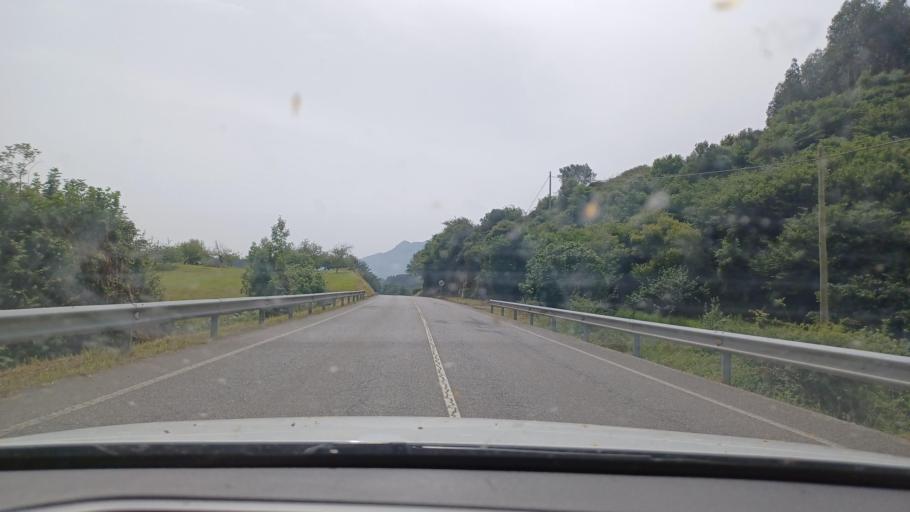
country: ES
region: Asturias
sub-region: Province of Asturias
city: Ribadesella
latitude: 43.4552
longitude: -5.0379
